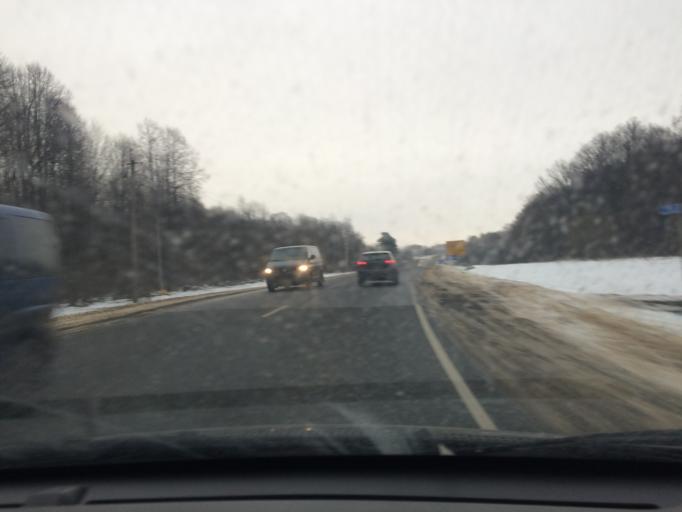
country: RU
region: Tula
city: Venev
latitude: 54.3368
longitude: 38.1374
